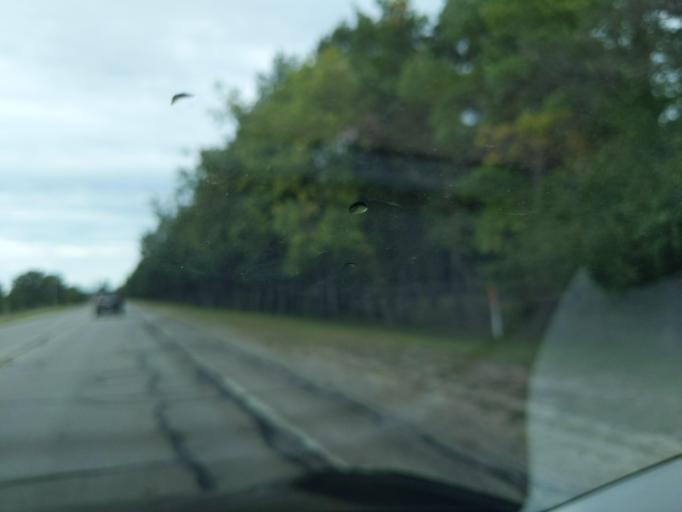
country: US
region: Michigan
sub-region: Grand Traverse County
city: Traverse City
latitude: 44.7531
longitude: -85.5865
